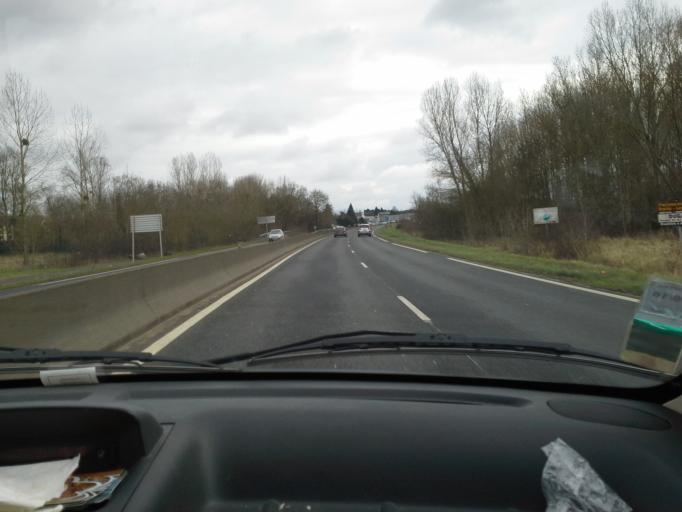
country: FR
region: Centre
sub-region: Departement du Loir-et-Cher
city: Vineuil
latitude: 47.5869
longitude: 1.3629
